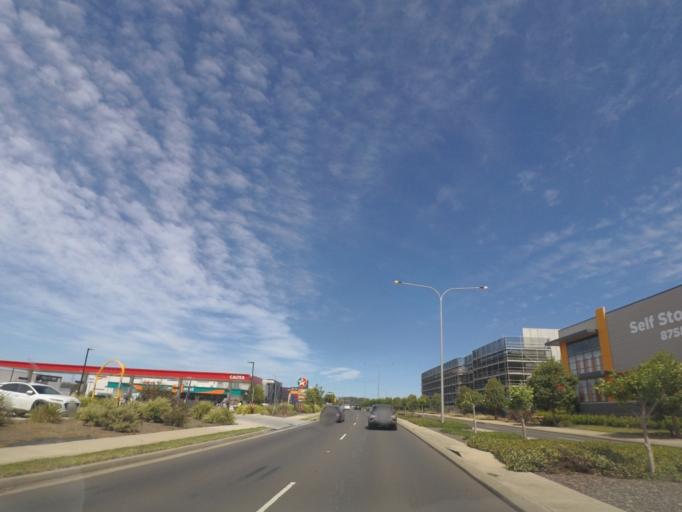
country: AU
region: New South Wales
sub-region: Camden
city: Narellan
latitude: -34.0207
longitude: 150.7627
